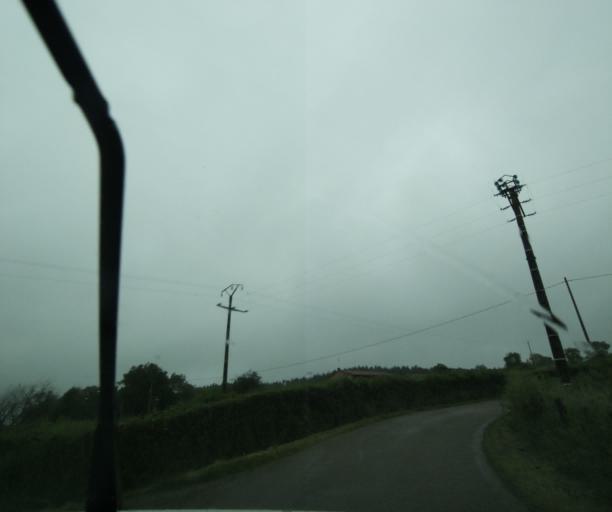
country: FR
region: Bourgogne
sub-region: Departement de Saone-et-Loire
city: Charolles
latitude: 46.3922
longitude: 4.3561
